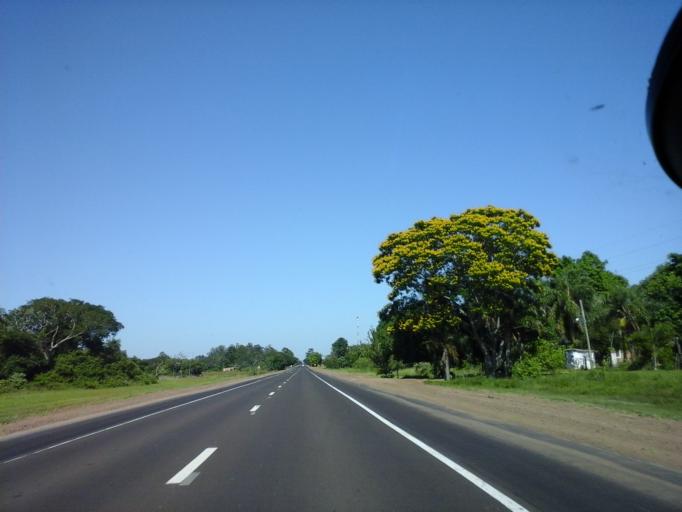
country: AR
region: Corrientes
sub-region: Departamento de Itati
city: Itati
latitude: -27.3665
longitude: -58.3267
